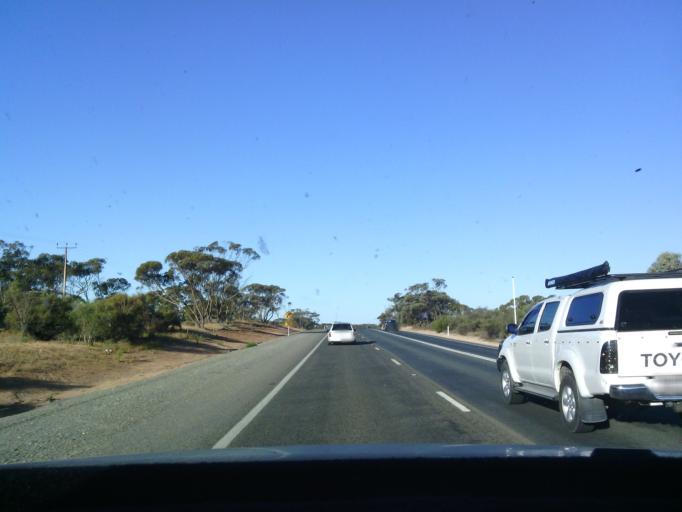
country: AU
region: South Australia
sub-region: Berri and Barmera
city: Berri
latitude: -34.2306
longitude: 140.6516
